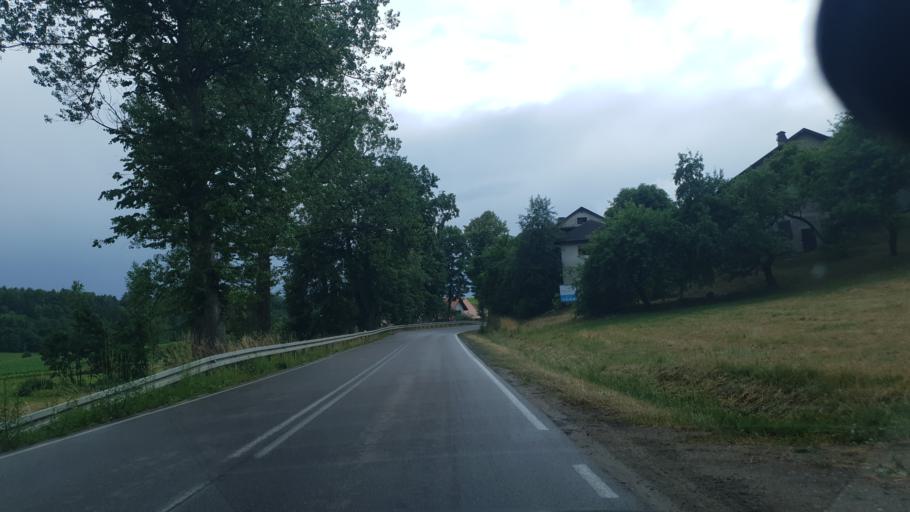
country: PL
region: Pomeranian Voivodeship
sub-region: Powiat kartuski
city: Chmielno
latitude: 54.2970
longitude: 18.1370
